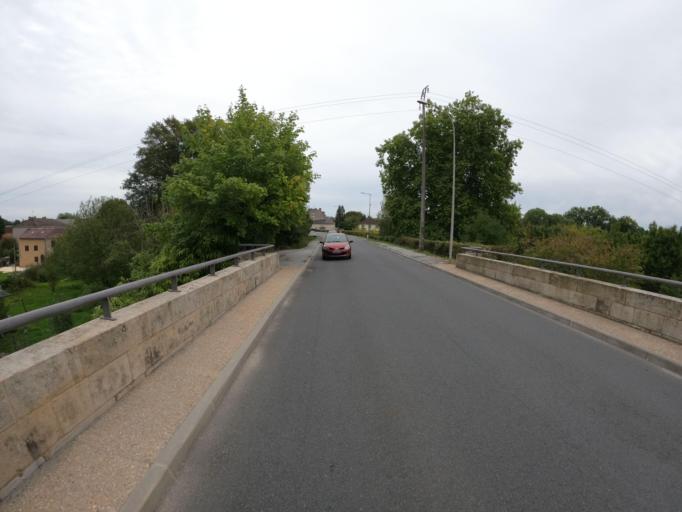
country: FR
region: Limousin
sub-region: Departement de la Haute-Vienne
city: Magnac-Laval
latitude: 46.2132
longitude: 1.1700
